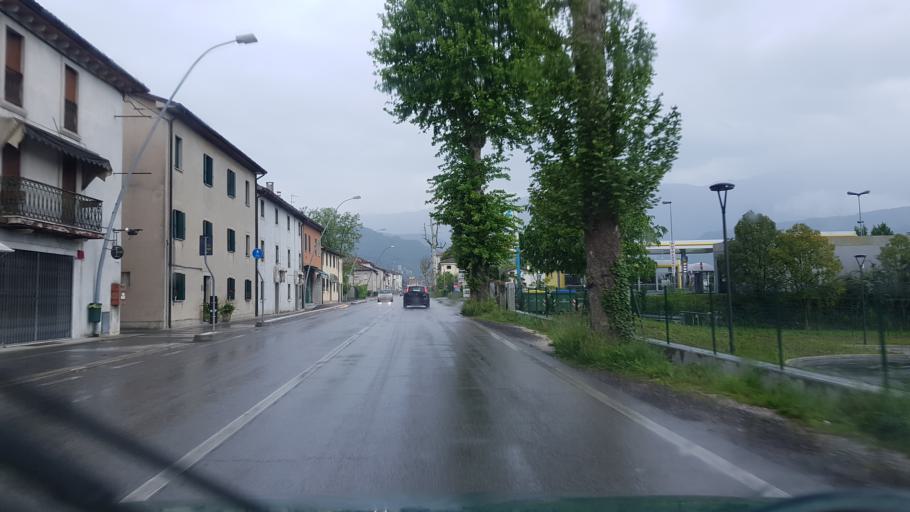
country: IT
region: Veneto
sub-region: Provincia di Treviso
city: Vittorio Veneto
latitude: 45.9664
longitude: 12.3188
